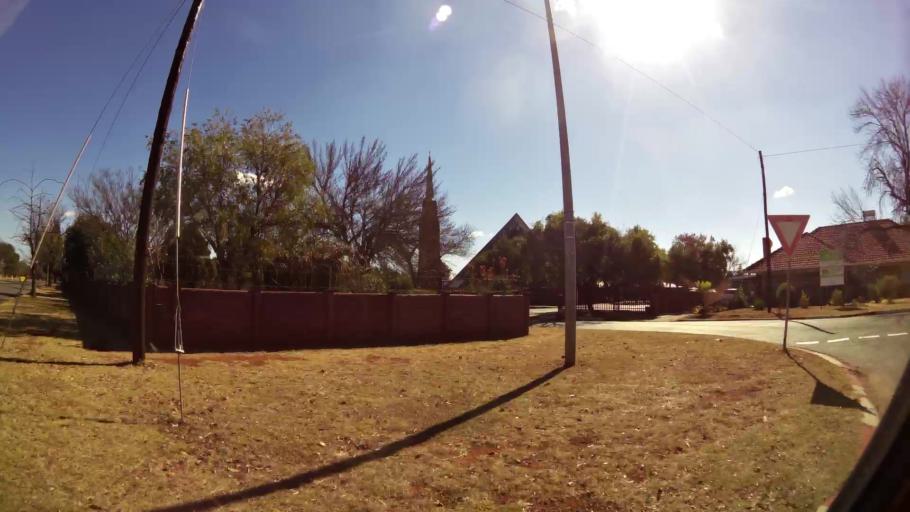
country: ZA
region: Gauteng
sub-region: West Rand District Municipality
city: Carletonville
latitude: -26.3523
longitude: 27.3892
